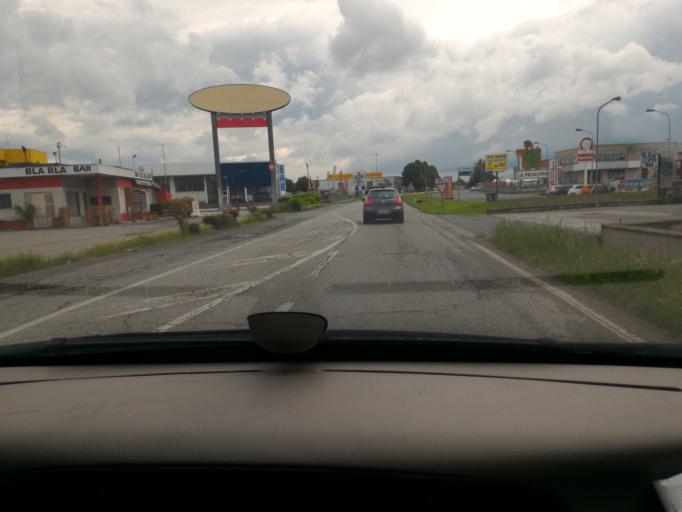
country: IT
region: Piedmont
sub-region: Provincia di Cuneo
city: Genola
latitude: 44.5971
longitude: 7.6593
